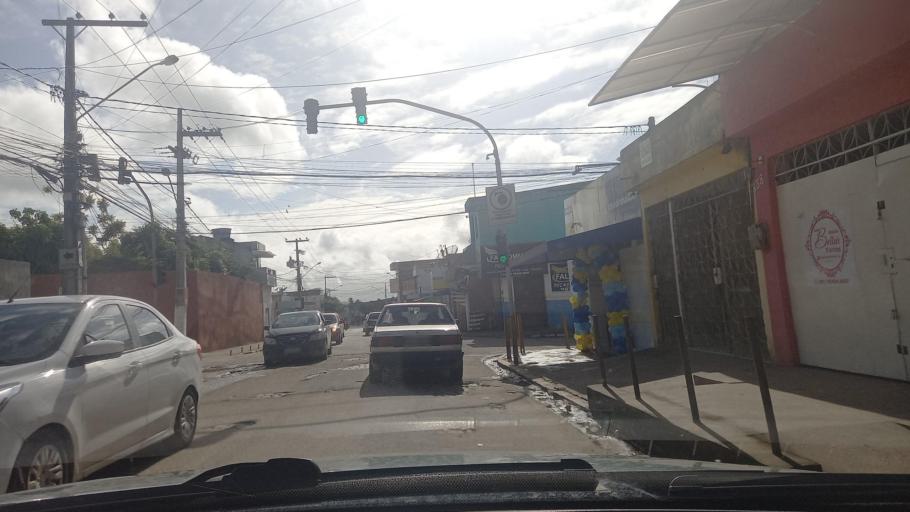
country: BR
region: Pernambuco
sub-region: Vitoria De Santo Antao
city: Vitoria de Santo Antao
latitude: -8.1096
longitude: -35.2867
